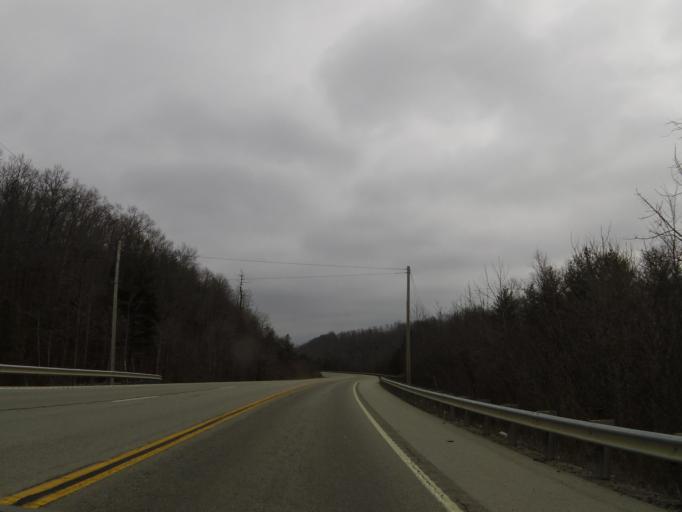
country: US
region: Tennessee
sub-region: Scott County
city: Huntsville
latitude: 36.3706
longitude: -84.5756
